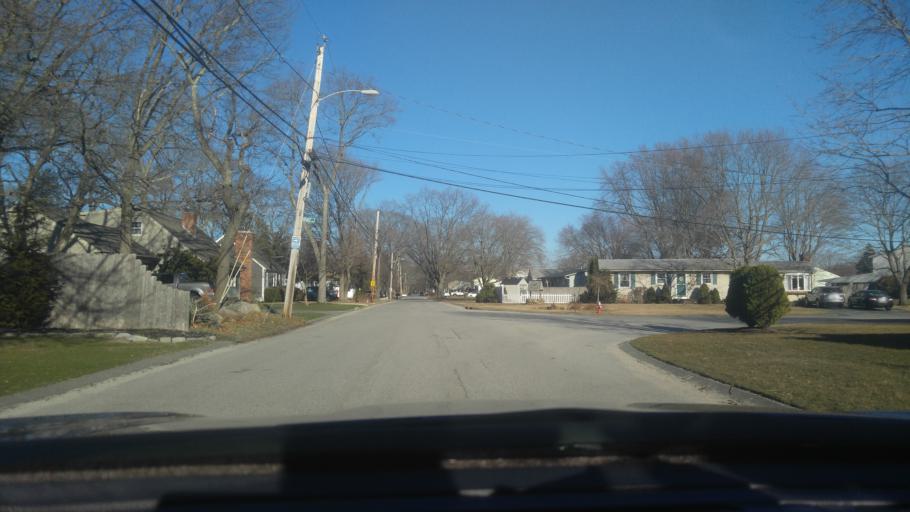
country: US
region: Rhode Island
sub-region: Kent County
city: Warwick
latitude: 41.6965
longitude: -71.4267
